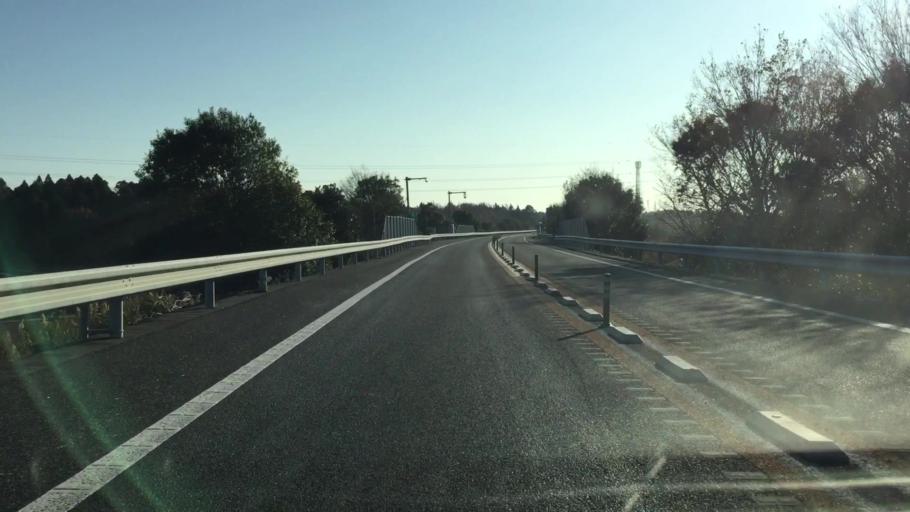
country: JP
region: Ibaraki
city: Ami
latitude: 35.9946
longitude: 140.2119
